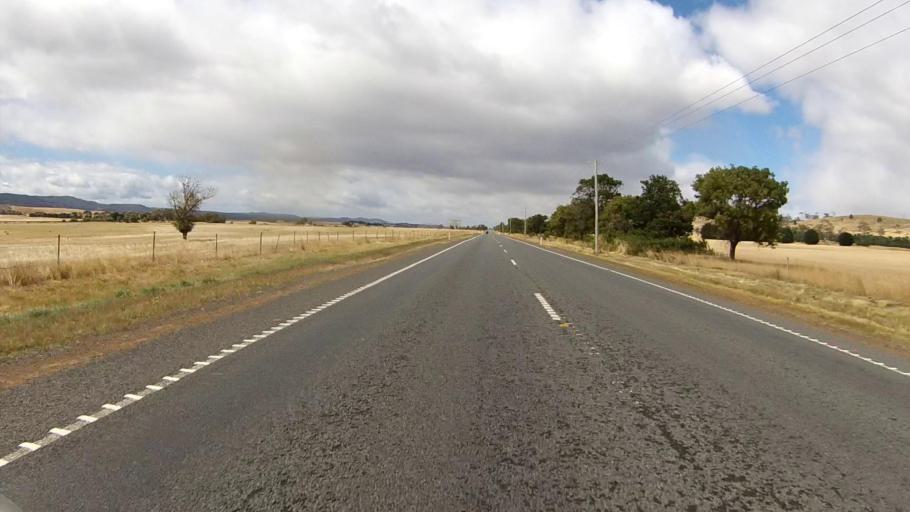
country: AU
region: Tasmania
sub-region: Northern Midlands
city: Evandale
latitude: -41.9636
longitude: 147.4993
